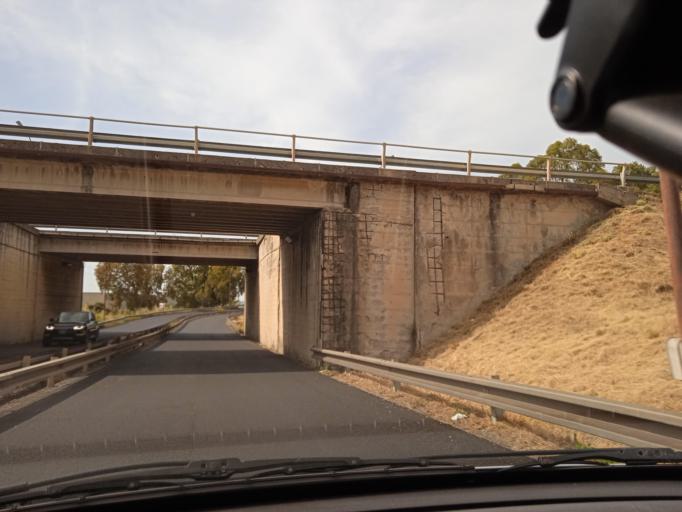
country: IT
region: Sicily
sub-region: Messina
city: San Filippo del Mela
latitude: 38.1917
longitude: 15.2743
